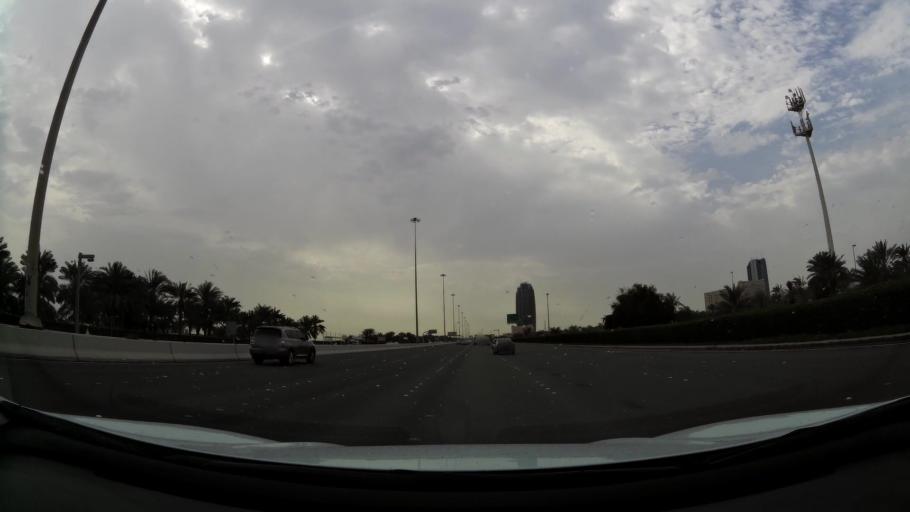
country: AE
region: Abu Dhabi
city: Abu Dhabi
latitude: 24.4659
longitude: 54.3962
